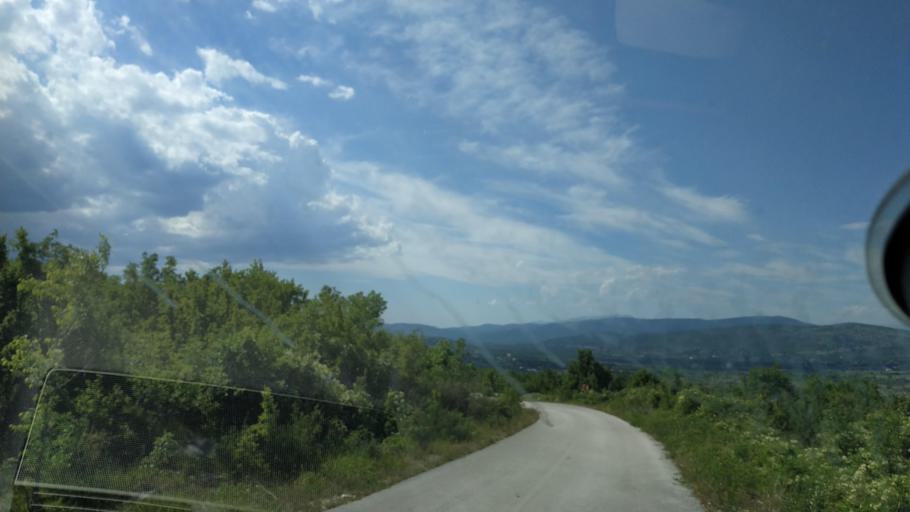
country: HR
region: Splitsko-Dalmatinska
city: Greda
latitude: 43.5801
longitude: 16.6550
